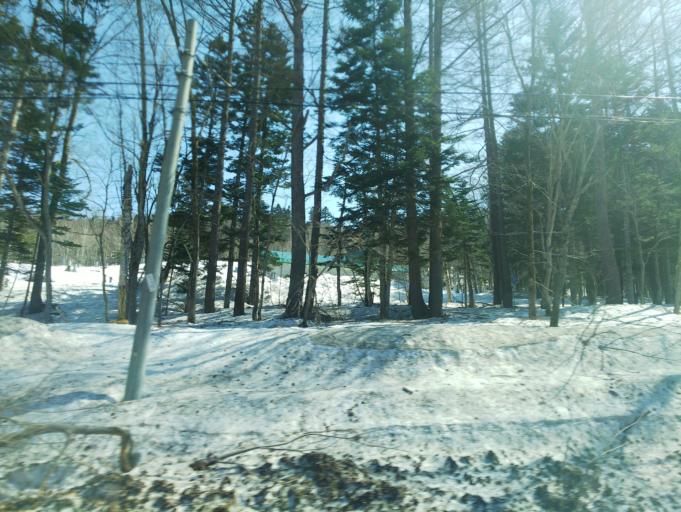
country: JP
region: Hokkaido
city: Nayoro
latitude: 44.7177
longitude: 142.2716
